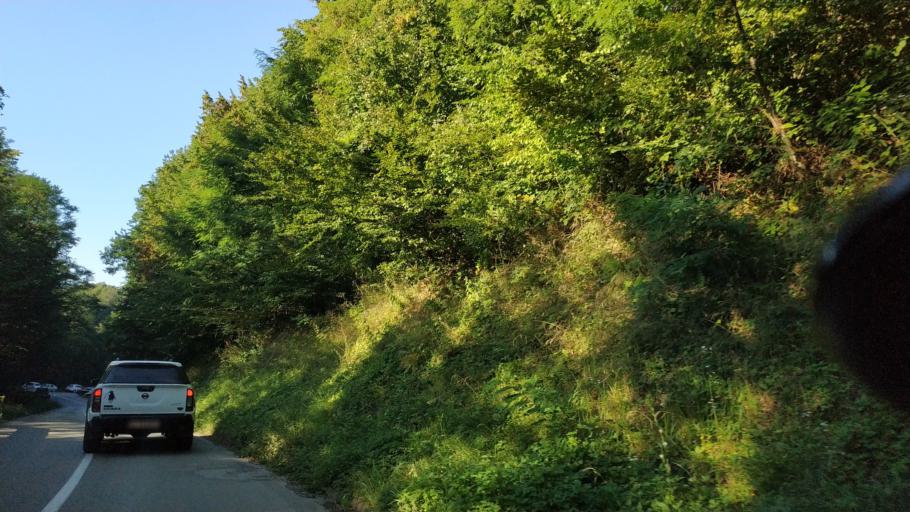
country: RS
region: Central Serbia
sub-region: Rasinski Okrug
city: Krusevac
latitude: 43.4572
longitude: 21.3591
